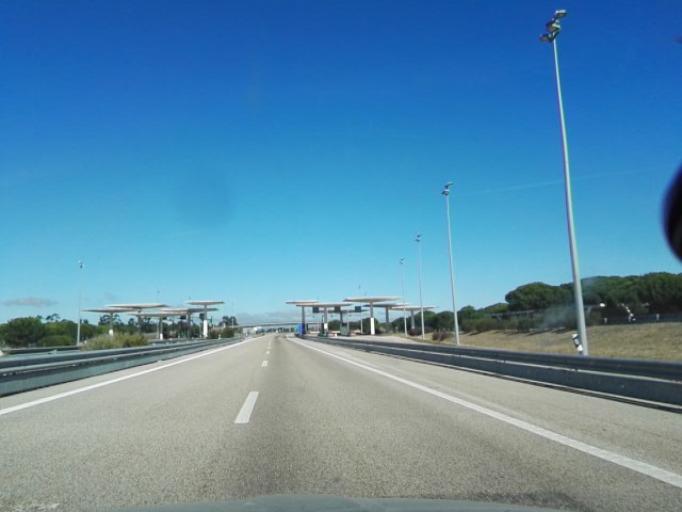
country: PT
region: Santarem
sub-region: Benavente
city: Benavente
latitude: 38.9571
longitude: -8.8294
